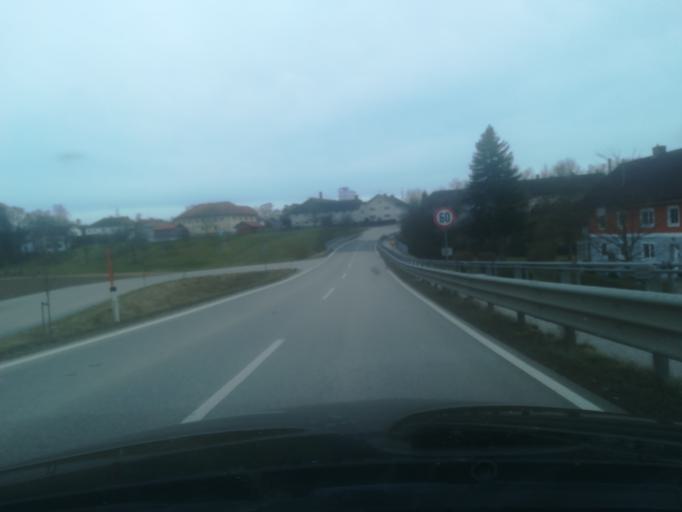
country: AT
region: Upper Austria
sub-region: Wels-Land
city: Neukirchen bei Lambach
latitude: 48.0945
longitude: 13.8374
